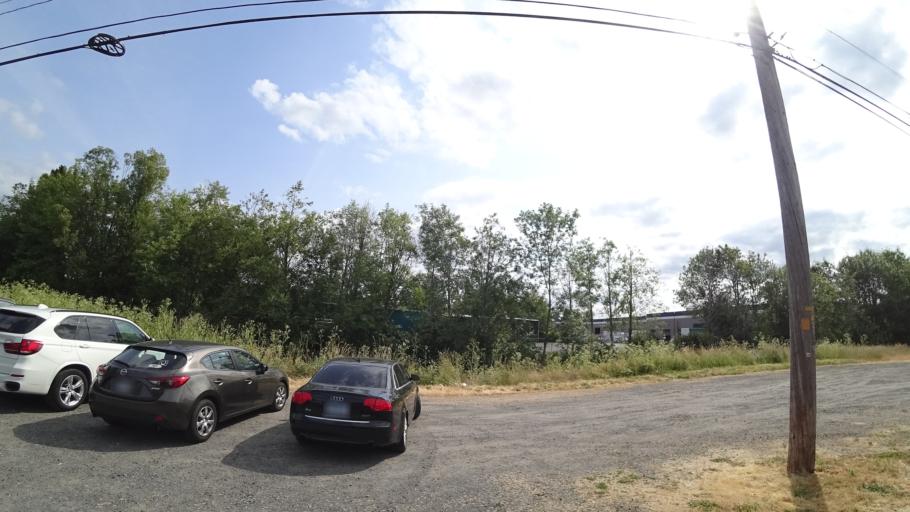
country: US
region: Washington
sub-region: Clark County
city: Vancouver
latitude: 45.5820
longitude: -122.6363
